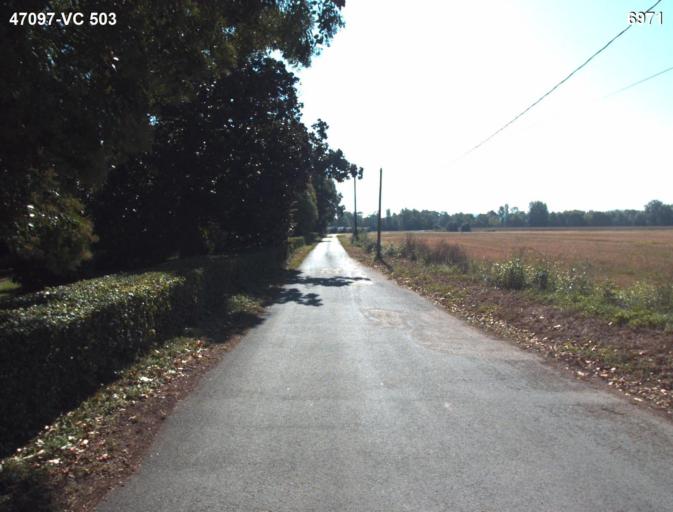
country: FR
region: Aquitaine
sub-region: Departement du Lot-et-Garonne
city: Port-Sainte-Marie
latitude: 44.2440
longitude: 0.3831
